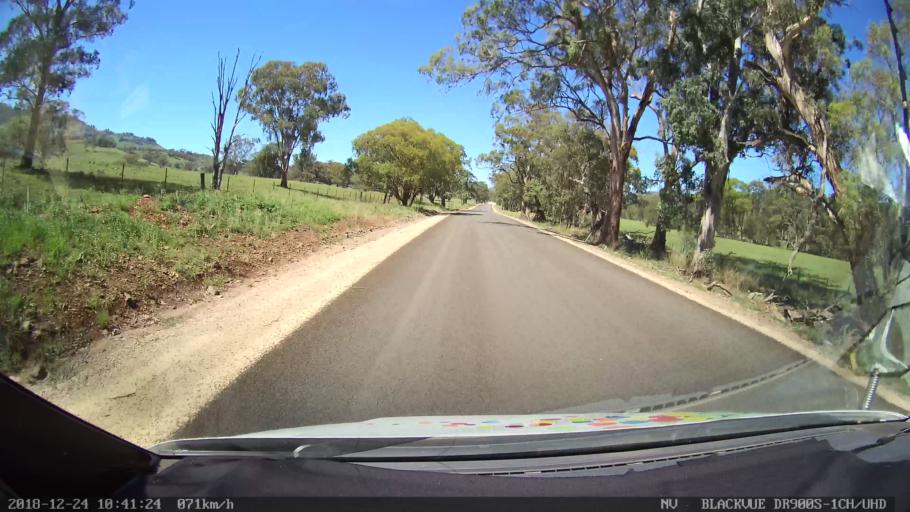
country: AU
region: New South Wales
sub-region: Upper Hunter Shire
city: Merriwa
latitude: -31.8686
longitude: 150.4594
